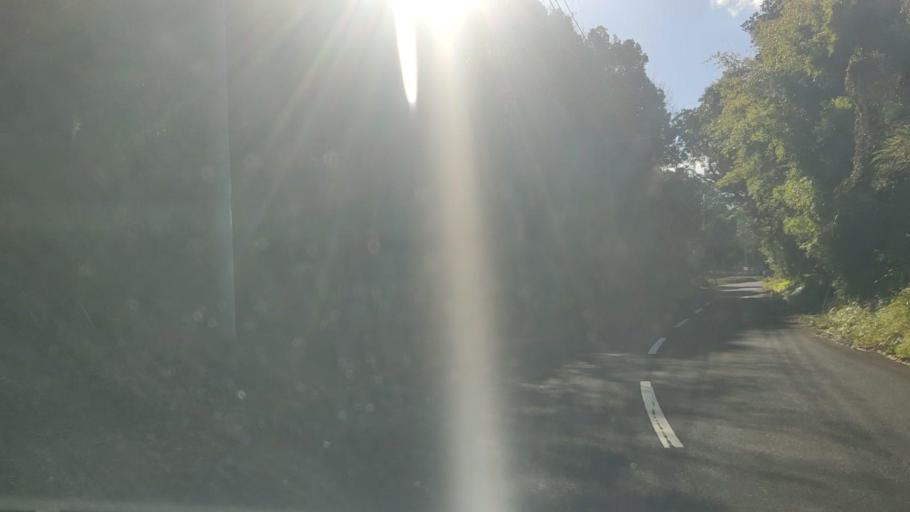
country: JP
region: Kagoshima
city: Kokubu-matsuki
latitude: 31.6668
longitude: 130.8229
